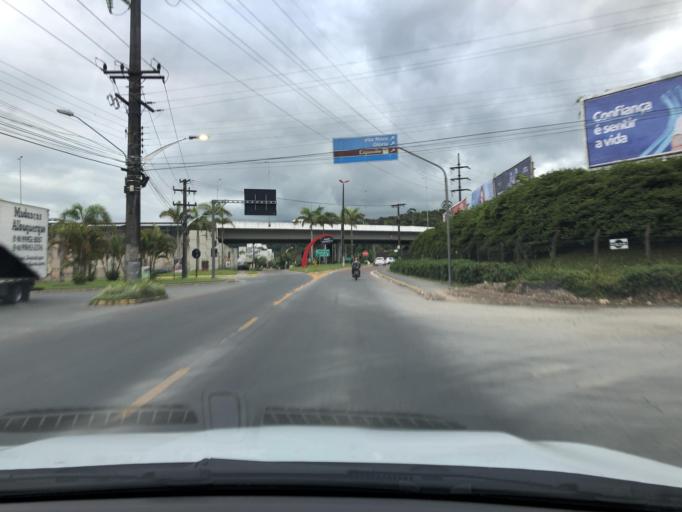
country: BR
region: Santa Catarina
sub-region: Joinville
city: Joinville
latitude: -26.3187
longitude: -48.8703
